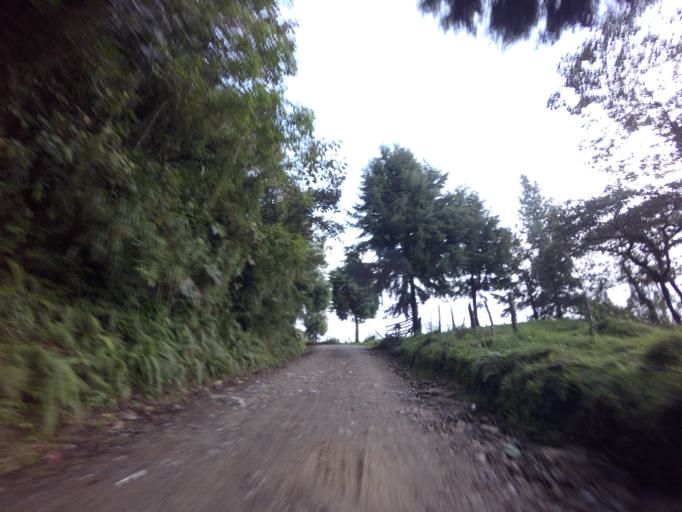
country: CO
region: Caldas
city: Pensilvania
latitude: 5.4204
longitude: -75.1363
